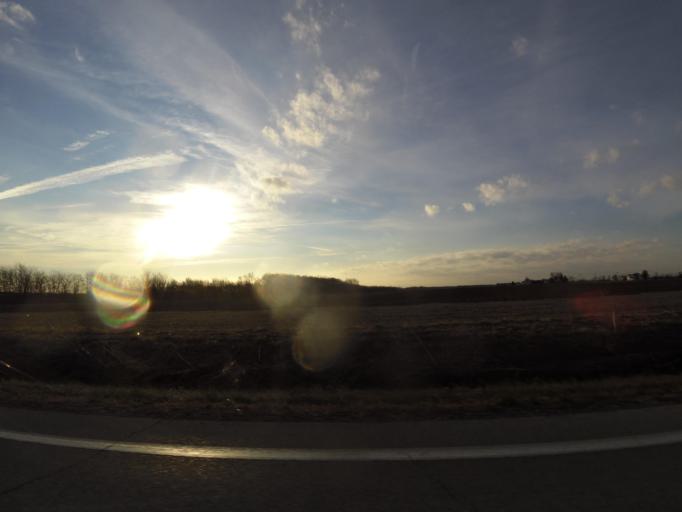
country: US
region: Illinois
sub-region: Fayette County
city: Vandalia
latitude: 38.9467
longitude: -89.1596
